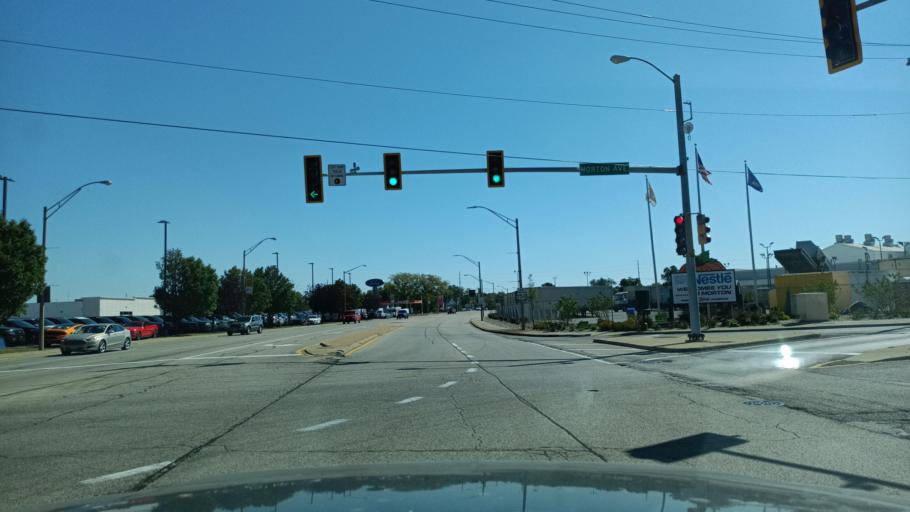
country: US
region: Illinois
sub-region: Tazewell County
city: Morton
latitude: 40.6160
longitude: -89.4645
